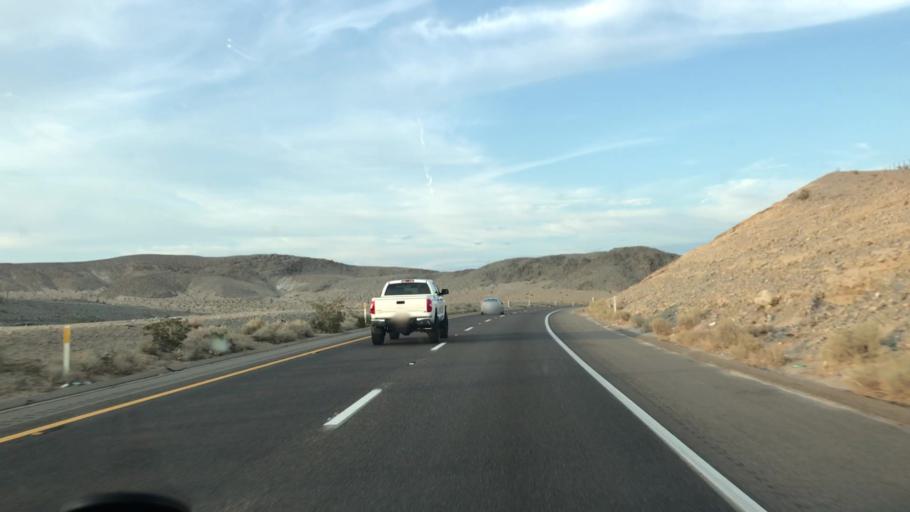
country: US
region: California
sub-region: San Bernardino County
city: Fort Irwin
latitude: 35.0774
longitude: -116.4021
